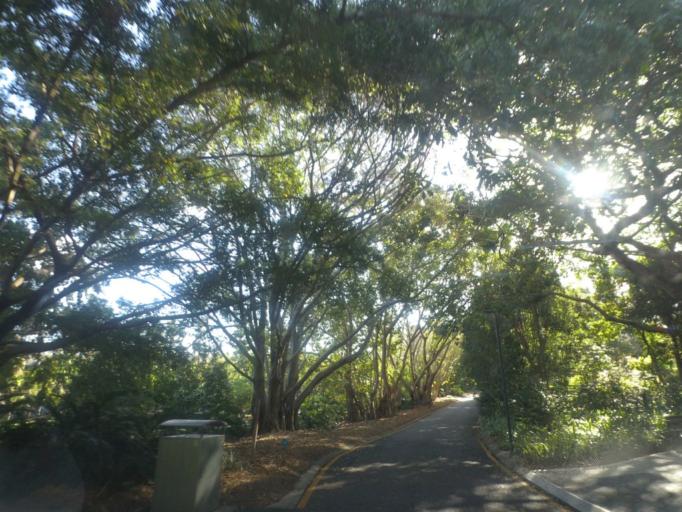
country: AU
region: Queensland
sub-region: Brisbane
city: Taringa
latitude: -27.4773
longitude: 152.9776
